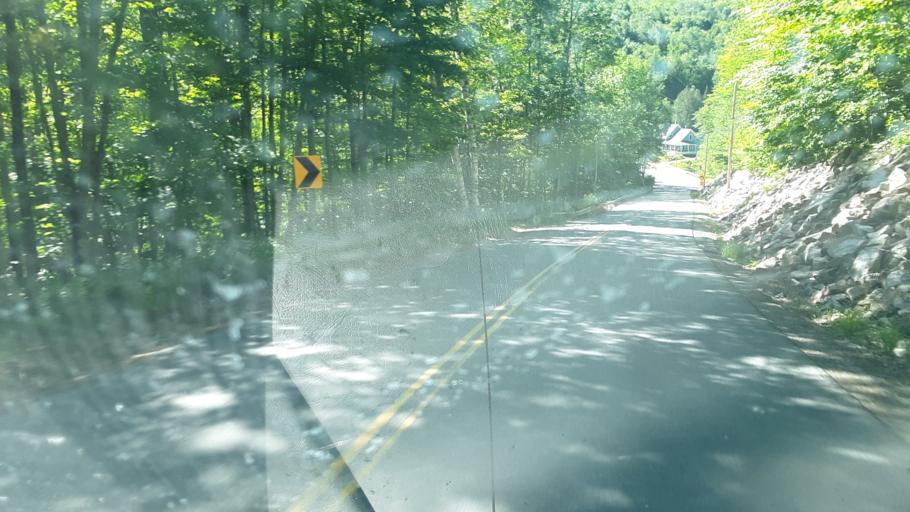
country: US
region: New Hampshire
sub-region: Grafton County
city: North Haverhill
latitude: 44.0982
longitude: -71.8883
